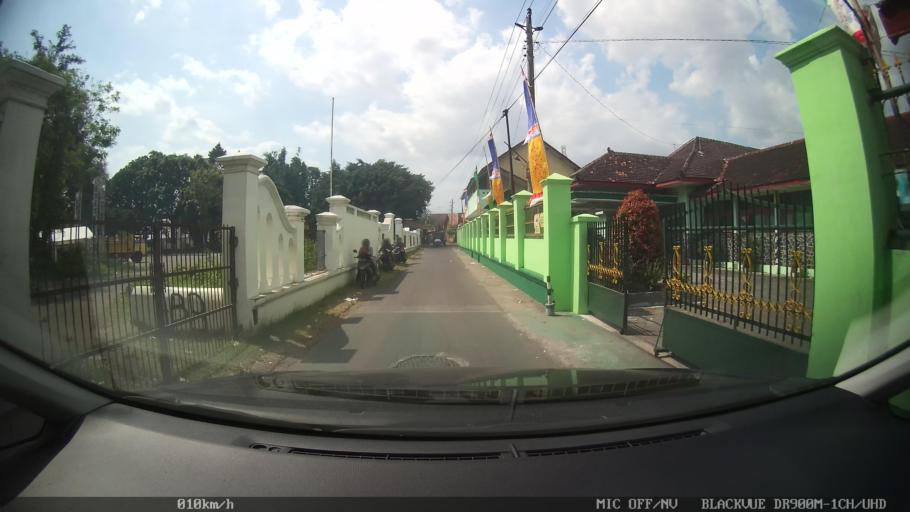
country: ID
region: Daerah Istimewa Yogyakarta
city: Kasihan
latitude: -7.8142
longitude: 110.3364
